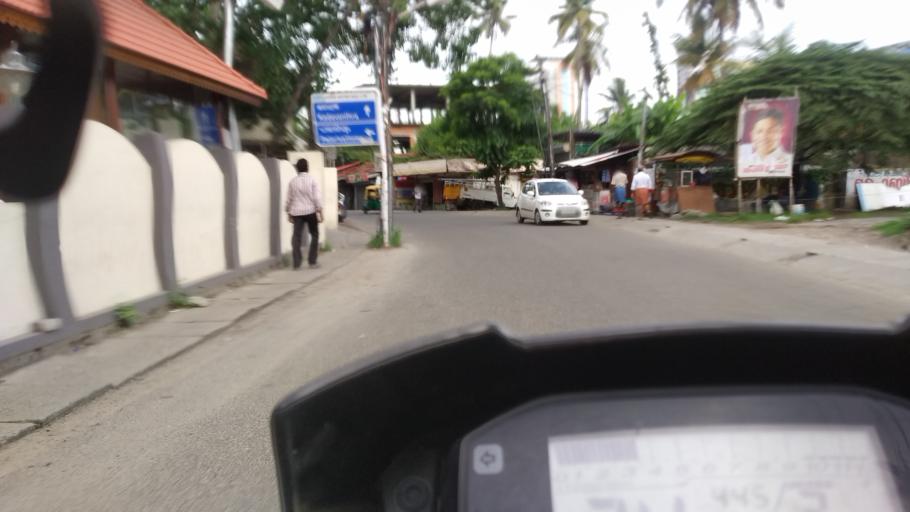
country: IN
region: Kerala
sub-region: Ernakulam
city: Cochin
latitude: 9.9964
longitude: 76.2914
